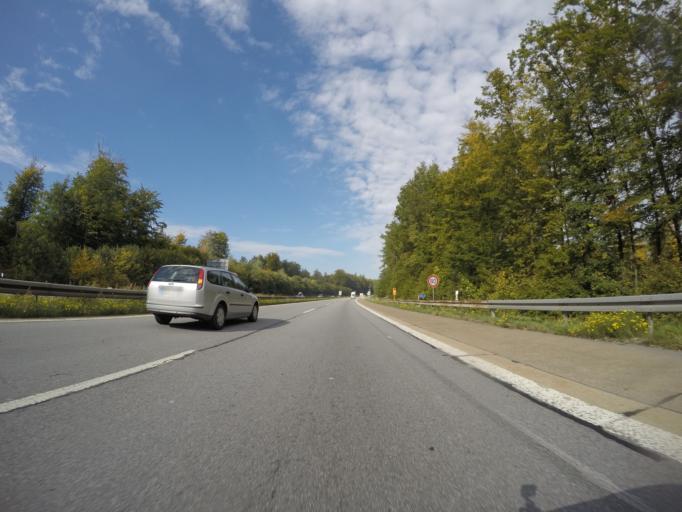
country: DE
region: Bavaria
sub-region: Regierungsbezirk Unterfranken
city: Weibersbrunn
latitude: 49.9050
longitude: 9.3757
